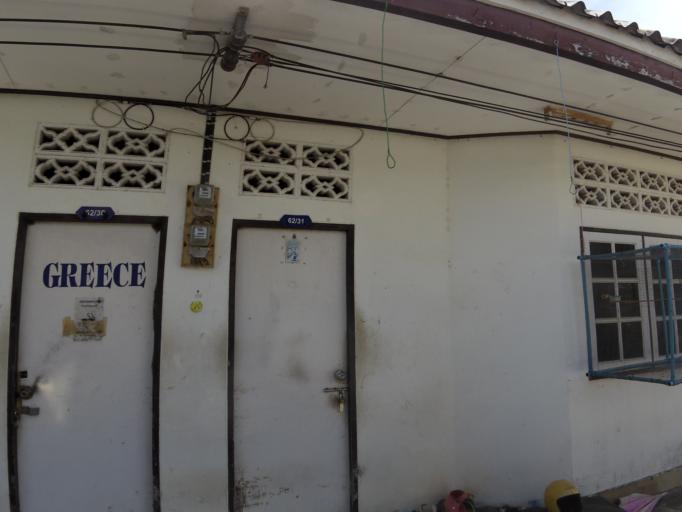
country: TH
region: Phuket
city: Ban Chalong
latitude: 7.8269
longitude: 98.3399
